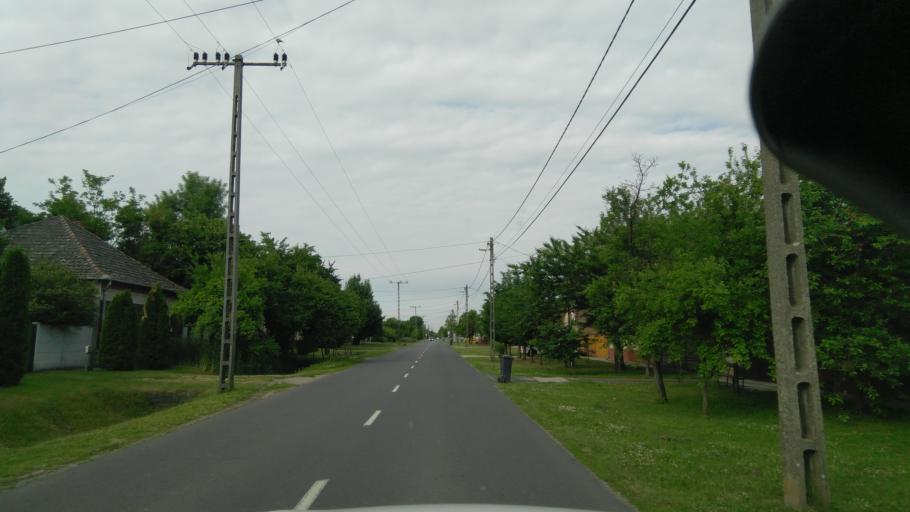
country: HU
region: Bekes
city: Ketegyhaza
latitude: 46.5456
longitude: 21.1777
